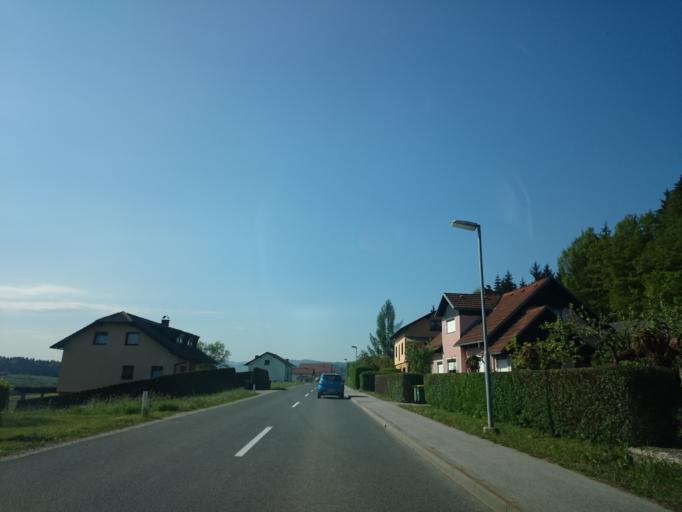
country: SI
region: Sentjur pri Celju
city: Sentjur
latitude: 46.2481
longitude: 15.3851
